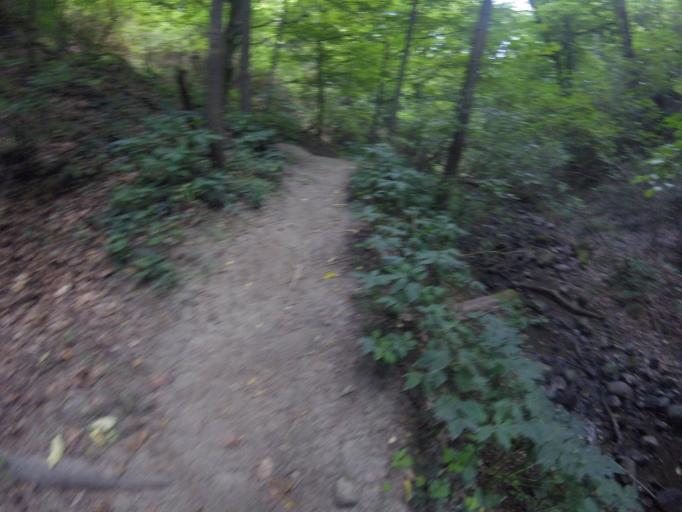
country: HU
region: Pest
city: Csobanka
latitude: 47.6709
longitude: 18.9673
